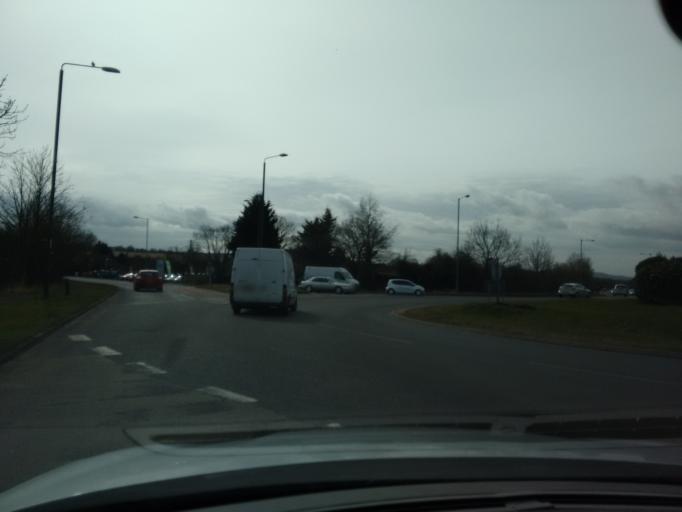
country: GB
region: England
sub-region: Worcestershire
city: Evesham
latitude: 52.0848
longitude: -1.9254
